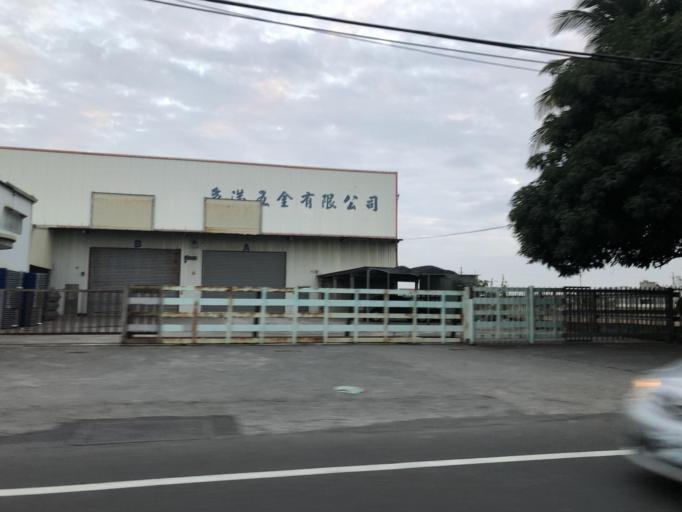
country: TW
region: Taiwan
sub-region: Tainan
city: Tainan
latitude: 23.0232
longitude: 120.3056
